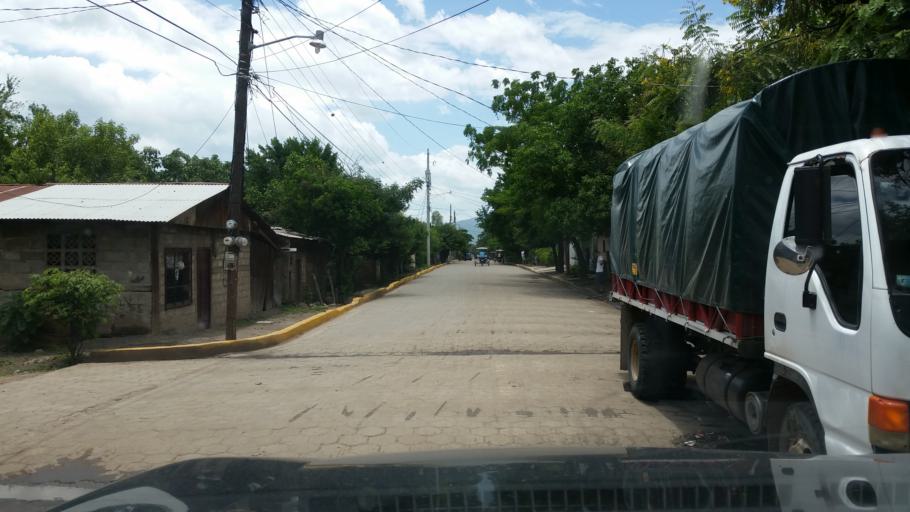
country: NI
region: Matagalpa
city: Ciudad Dario
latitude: 12.8558
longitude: -86.0923
